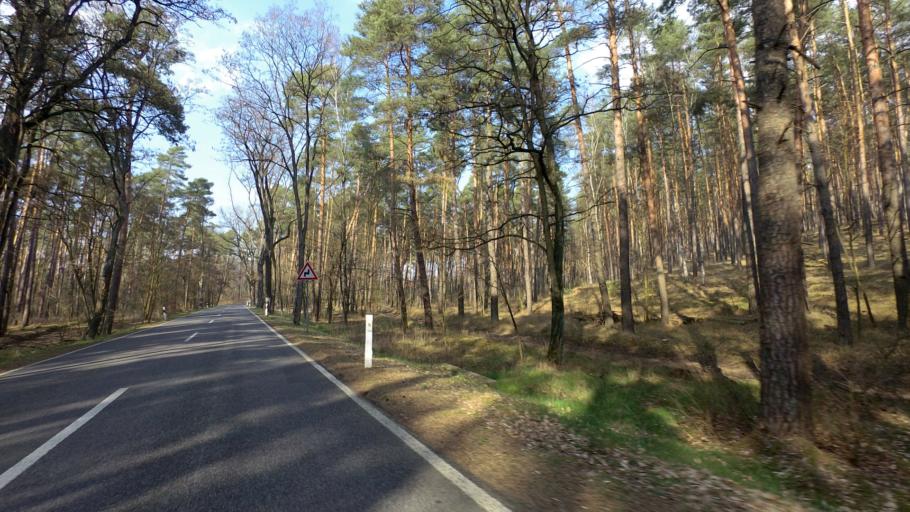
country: DE
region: Brandenburg
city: Dahme
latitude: 51.9368
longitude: 13.4462
